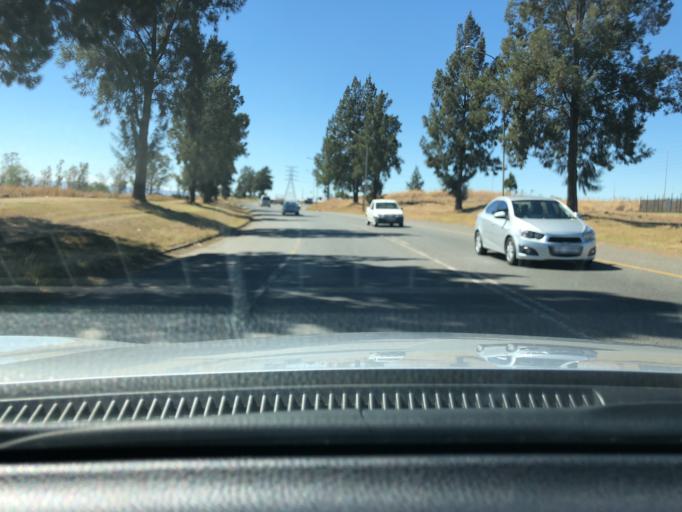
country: ZA
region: KwaZulu-Natal
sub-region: Amajuba District Municipality
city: Newcastle
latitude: -27.7613
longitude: 29.9588
